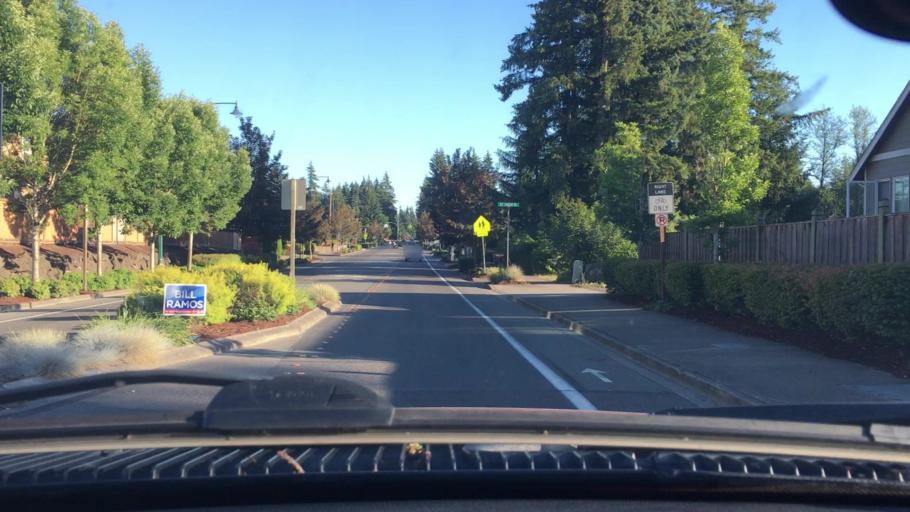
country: US
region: Washington
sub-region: King County
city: Maple Valley
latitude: 47.3867
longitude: -122.0481
